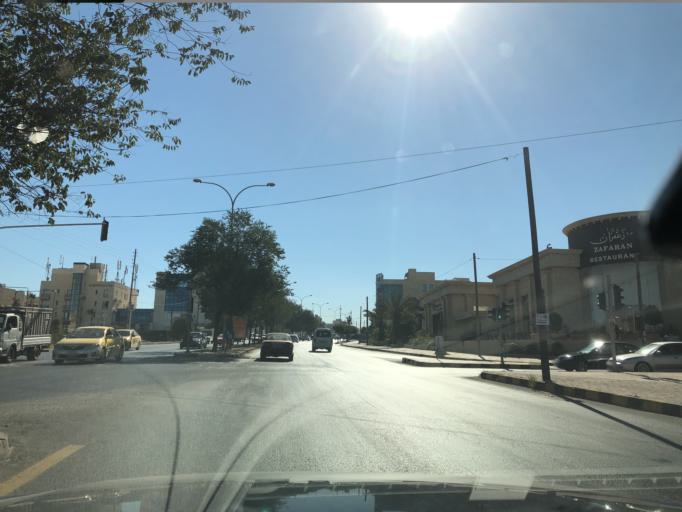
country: JO
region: Amman
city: Al Jubayhah
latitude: 31.9735
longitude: 35.8713
